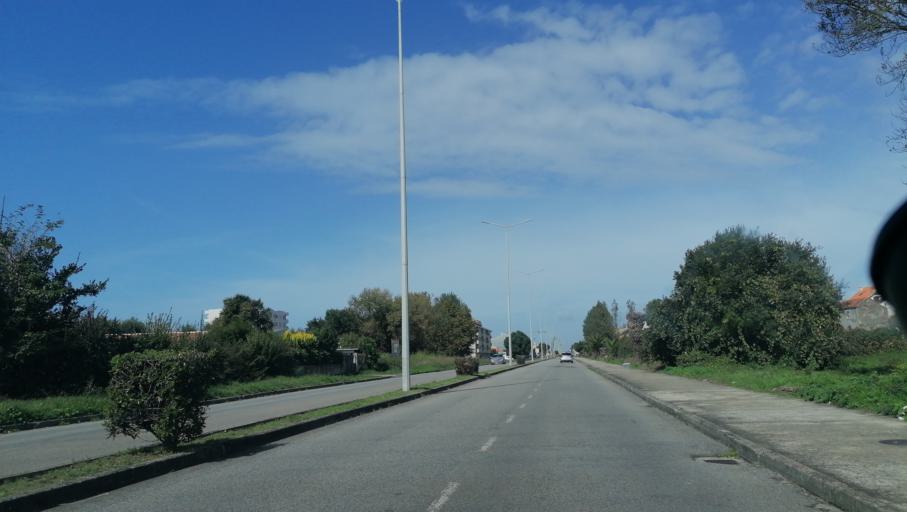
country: PT
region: Aveiro
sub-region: Espinho
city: Espinho
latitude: 41.0011
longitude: -8.6343
